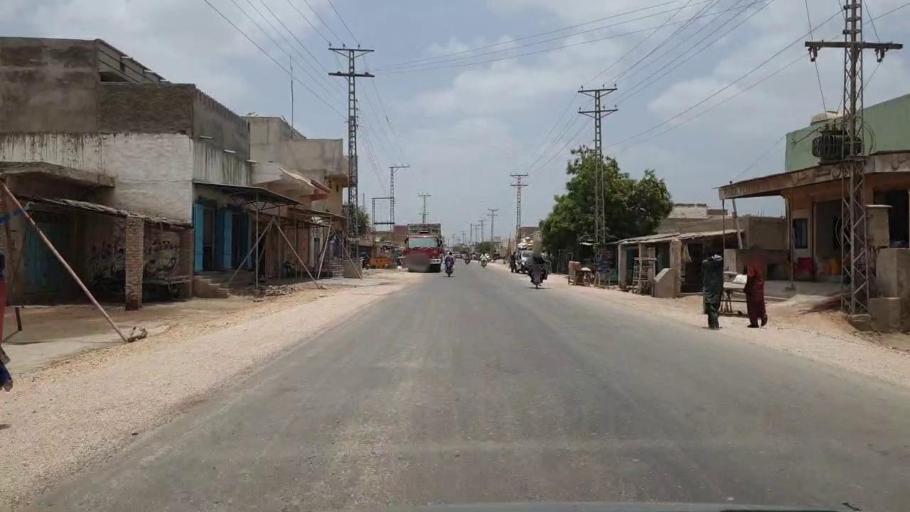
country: PK
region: Sindh
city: Naukot
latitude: 24.8526
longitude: 69.4075
